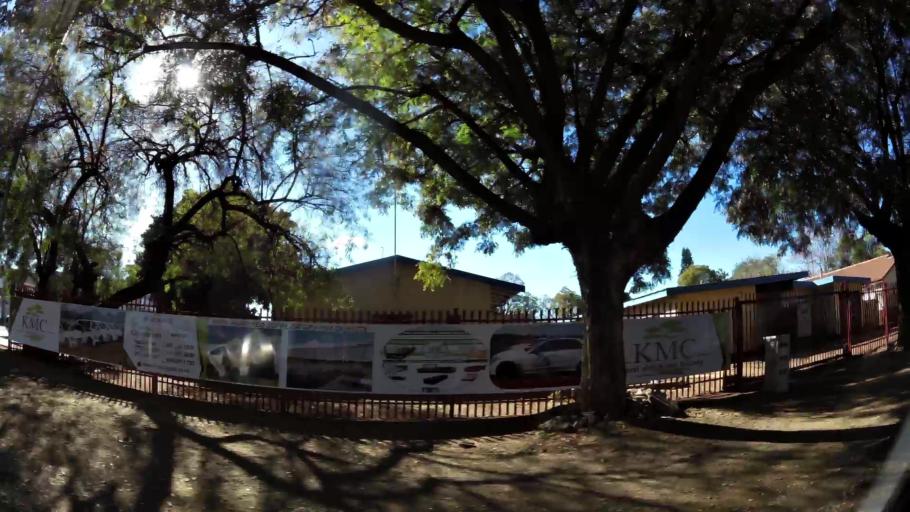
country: ZA
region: Limpopo
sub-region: Capricorn District Municipality
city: Polokwane
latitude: -23.9083
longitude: 29.4465
